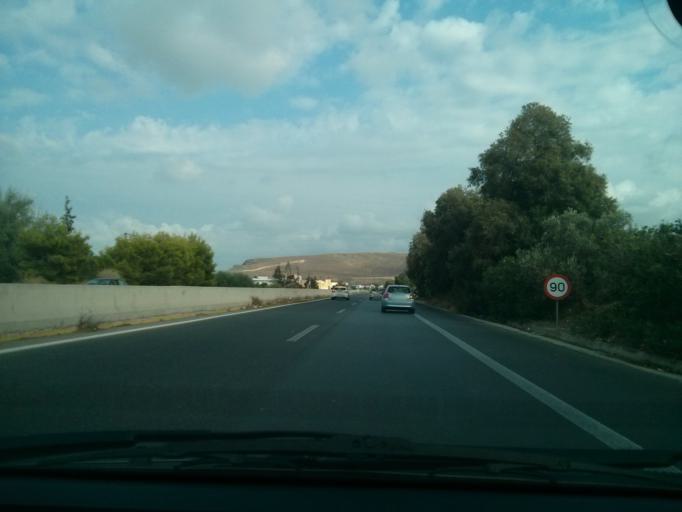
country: GR
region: Crete
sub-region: Nomos Irakleiou
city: Kokkini Hani
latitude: 35.3298
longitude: 25.2458
